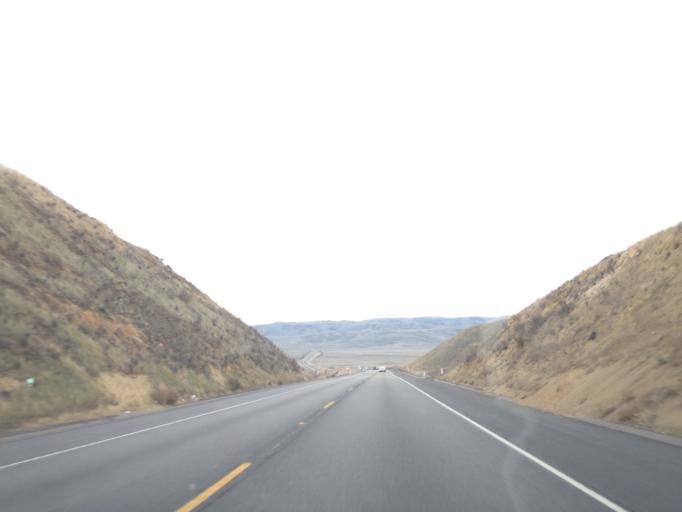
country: US
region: California
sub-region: San Luis Obispo County
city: Shandon
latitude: 35.7417
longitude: -120.2500
